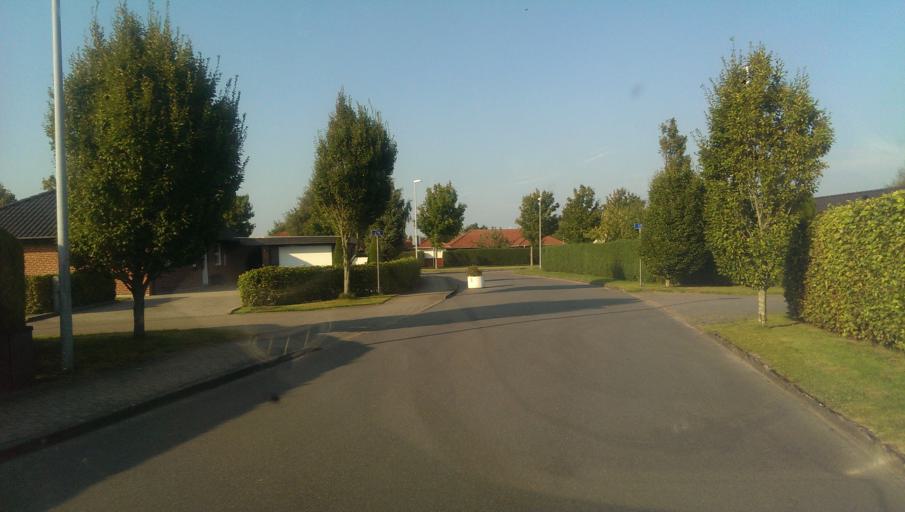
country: DK
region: South Denmark
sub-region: Esbjerg Kommune
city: Bramming
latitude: 55.4754
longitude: 8.7131
